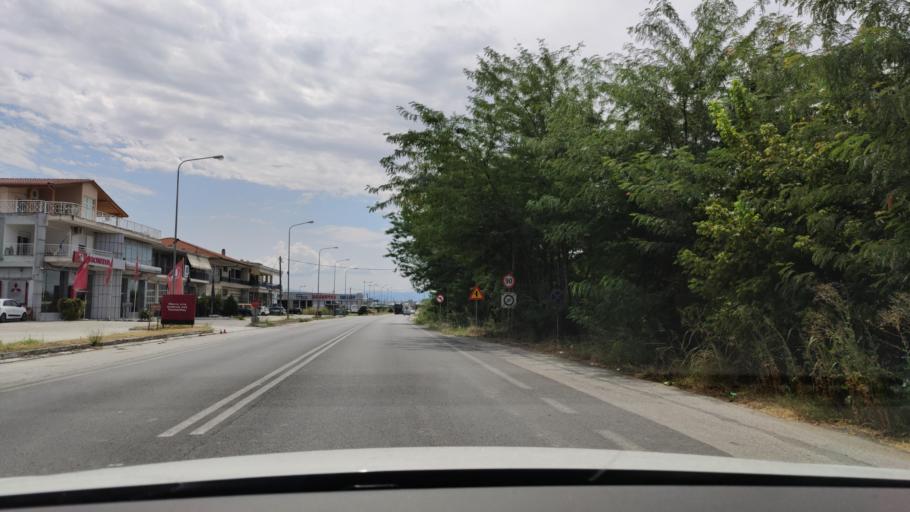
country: GR
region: Central Macedonia
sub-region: Nomos Serron
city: Serres
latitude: 41.0696
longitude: 23.5405
